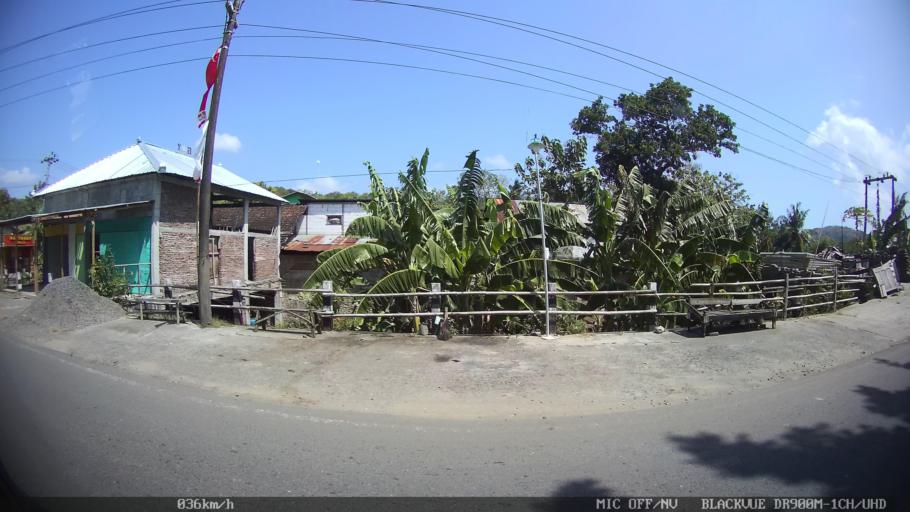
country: ID
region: Daerah Istimewa Yogyakarta
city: Pundong
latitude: -7.9521
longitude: 110.3802
